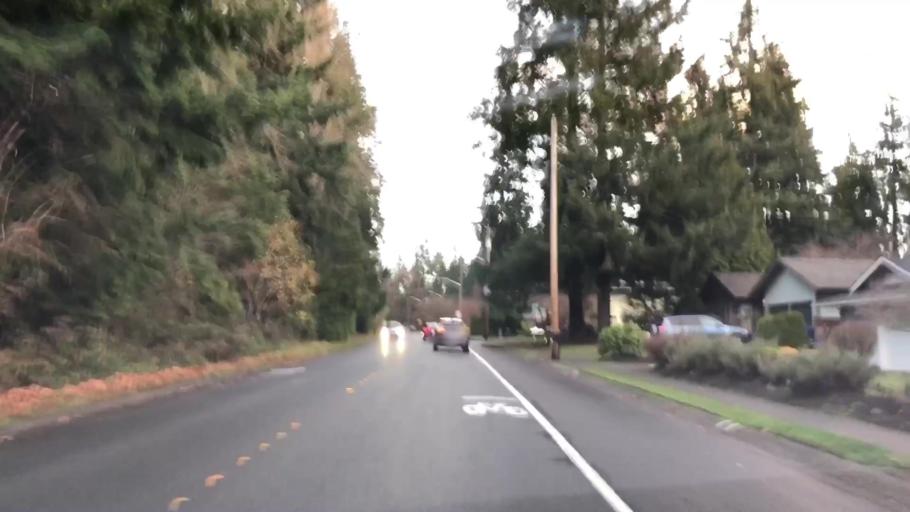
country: US
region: Washington
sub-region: King County
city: West Lake Sammamish
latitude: 47.5849
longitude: -122.1238
